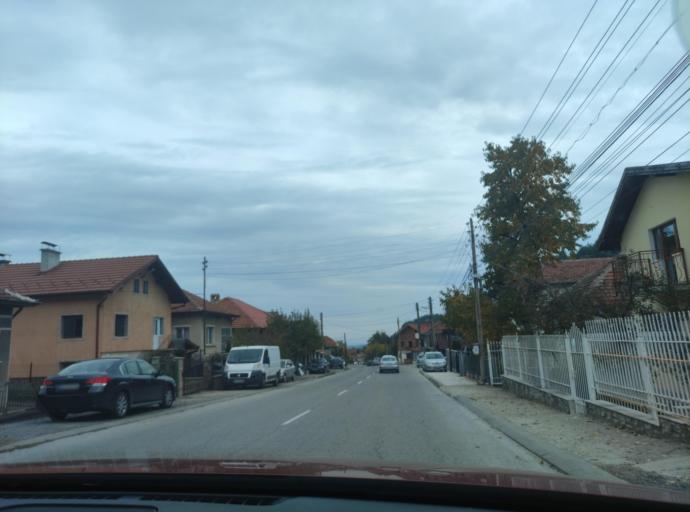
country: BG
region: Montana
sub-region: Obshtina Berkovitsa
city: Berkovitsa
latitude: 43.1910
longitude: 23.1595
